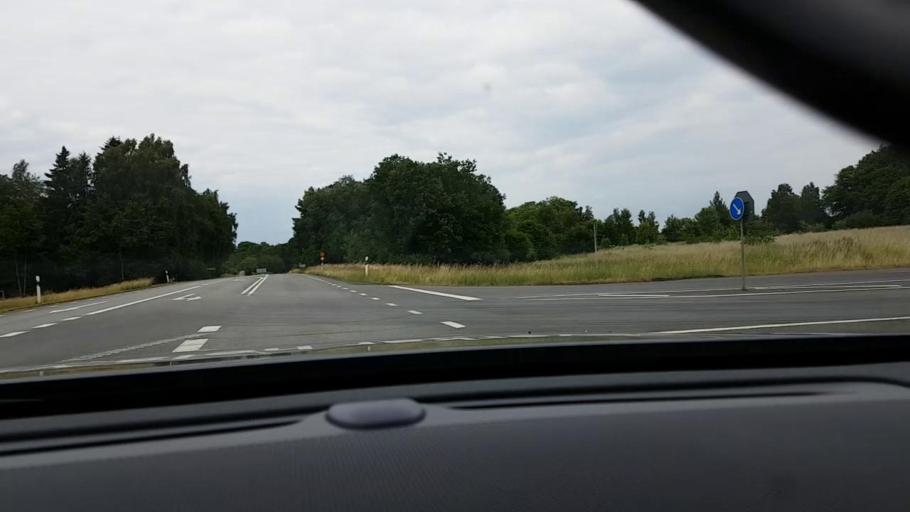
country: SE
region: Skane
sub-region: Hassleholms Kommun
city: Hassleholm
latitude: 56.1411
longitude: 13.8033
